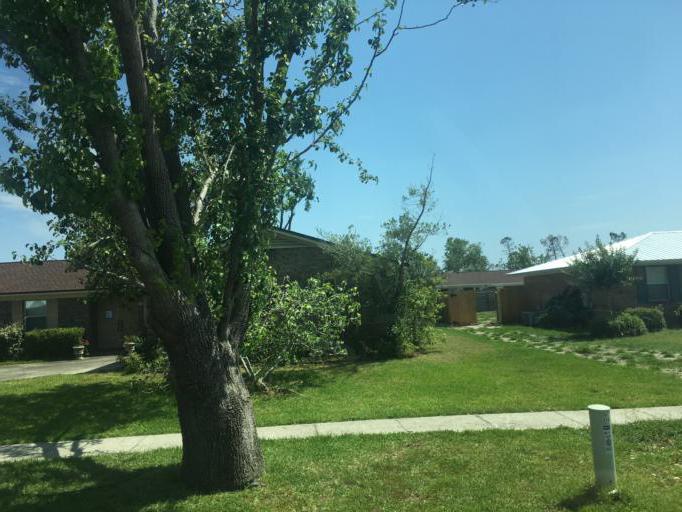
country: US
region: Florida
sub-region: Bay County
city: Lynn Haven
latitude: 30.2206
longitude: -85.6536
